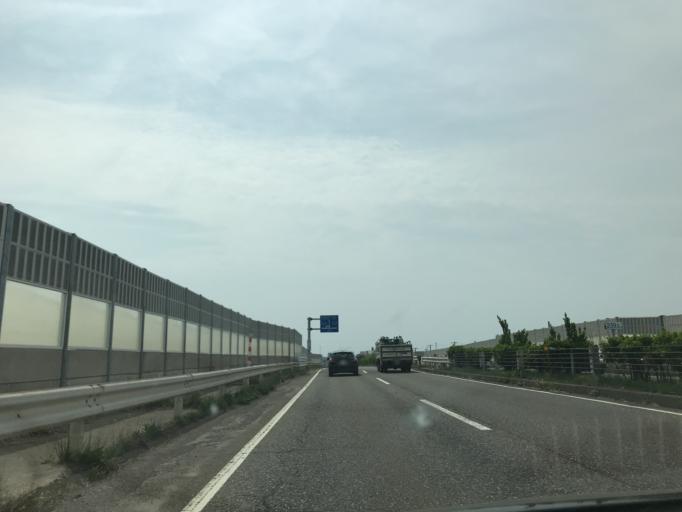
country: JP
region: Niigata
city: Kameda-honcho
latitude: 37.8890
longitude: 139.0763
